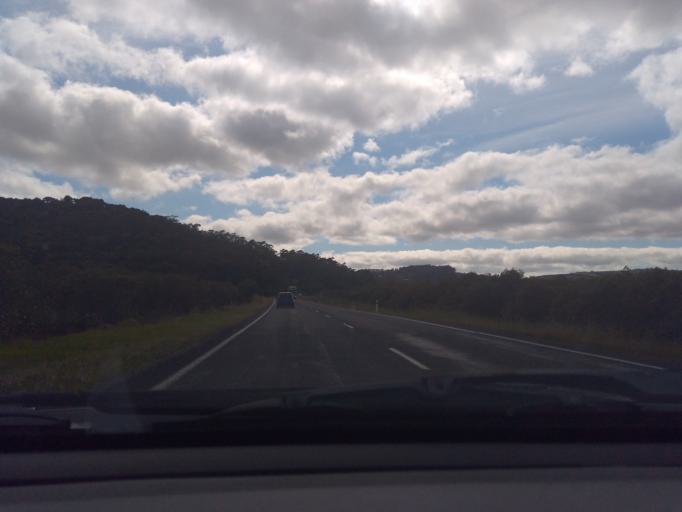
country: NZ
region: Northland
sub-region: Far North District
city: Taipa
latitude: -35.0117
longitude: 173.5448
